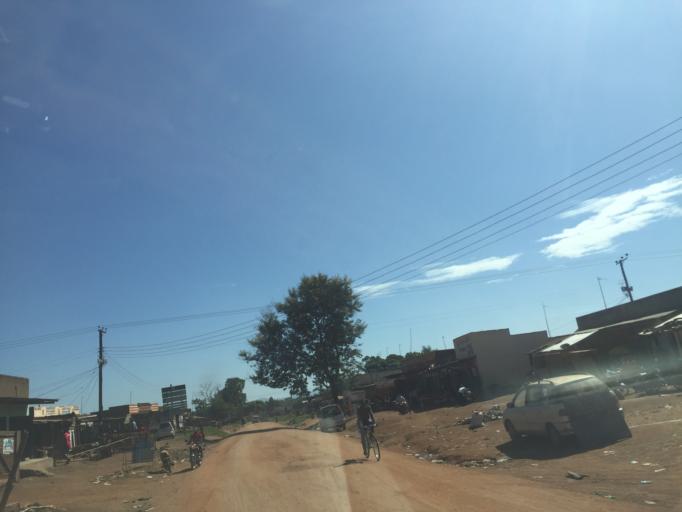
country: UG
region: Central Region
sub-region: Luwero District
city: Luwero
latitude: 0.8337
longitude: 32.5000
